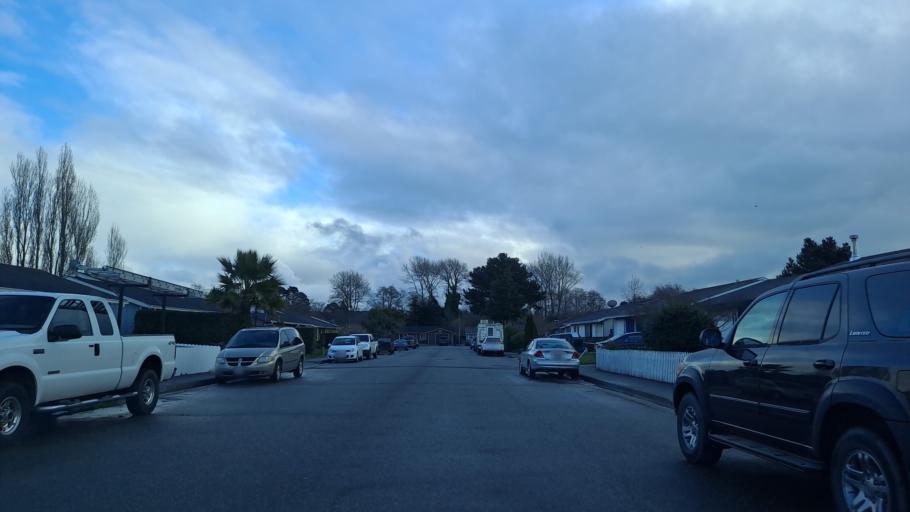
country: US
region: California
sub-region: Humboldt County
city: Fortuna
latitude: 40.5837
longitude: -124.1420
